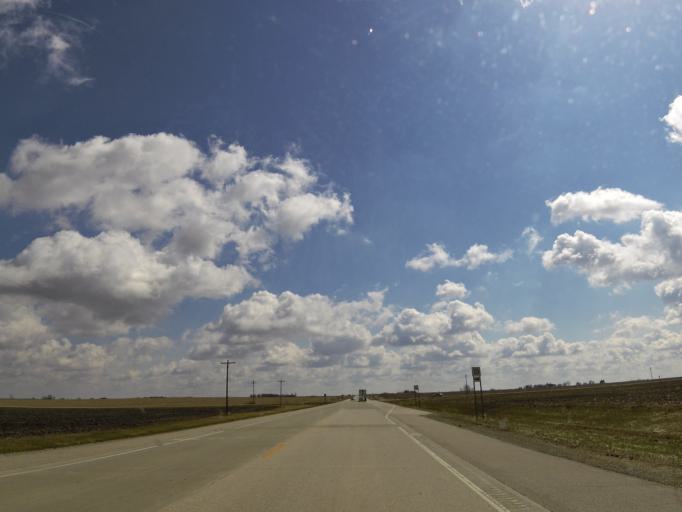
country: US
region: Minnesota
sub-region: Dodge County
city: Dodge Center
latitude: 44.1047
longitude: -92.8995
